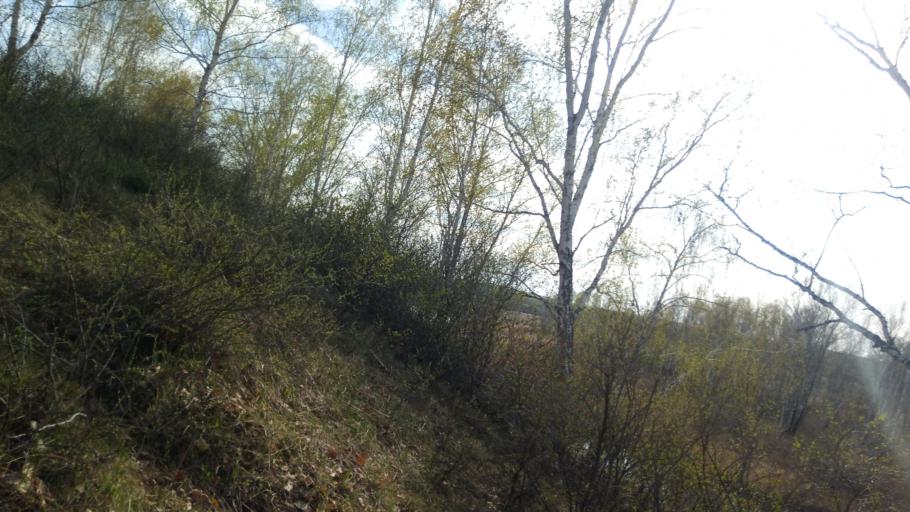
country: RU
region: Chelyabinsk
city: Poletayevo
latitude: 55.0314
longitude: 61.0743
